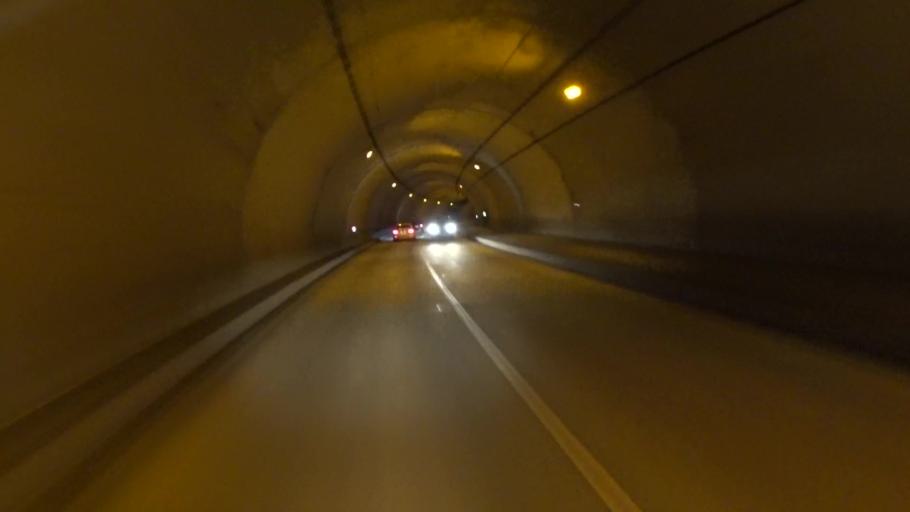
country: JP
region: Hyogo
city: Toyooka
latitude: 35.5773
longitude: 134.9983
